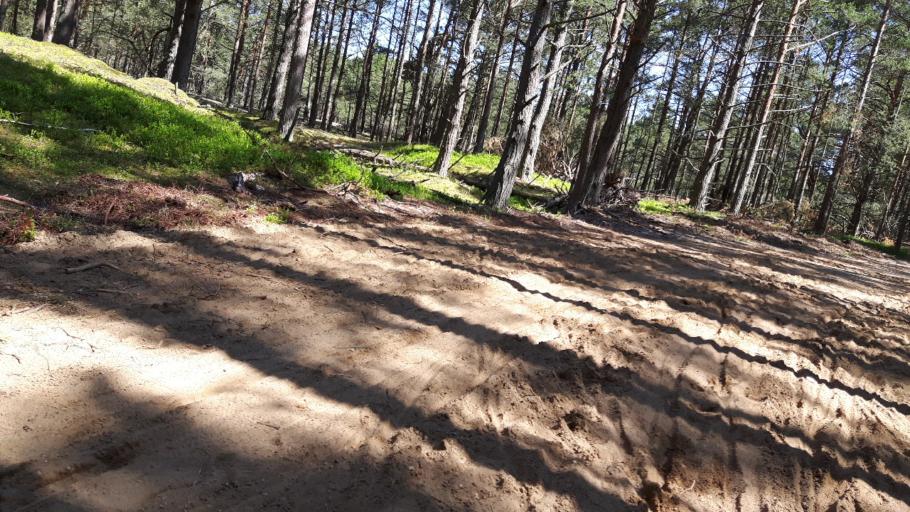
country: PL
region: Pomeranian Voivodeship
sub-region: Powiat slupski
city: Smoldzino
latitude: 54.6775
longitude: 17.1352
